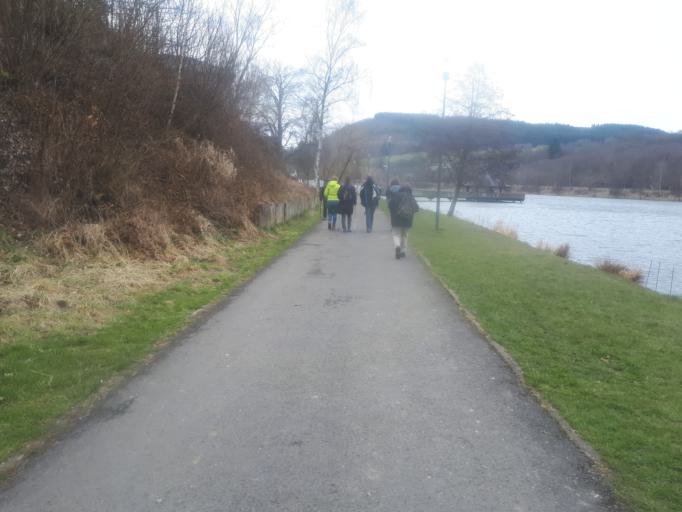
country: BE
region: Wallonia
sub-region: Province du Luxembourg
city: Vielsalm
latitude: 50.2857
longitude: 5.9144
